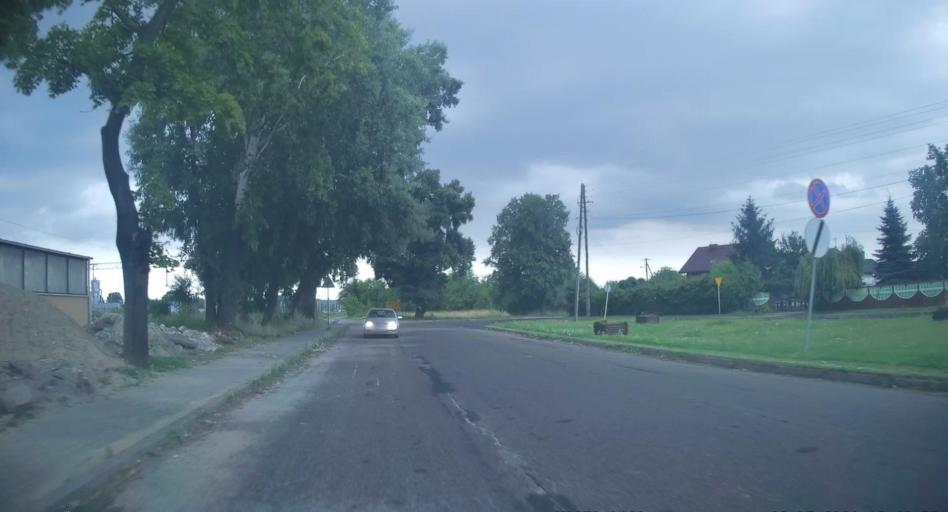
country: PL
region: Lodz Voivodeship
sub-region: Powiat brzezinski
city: Rogow
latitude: 51.8180
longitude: 19.8868
